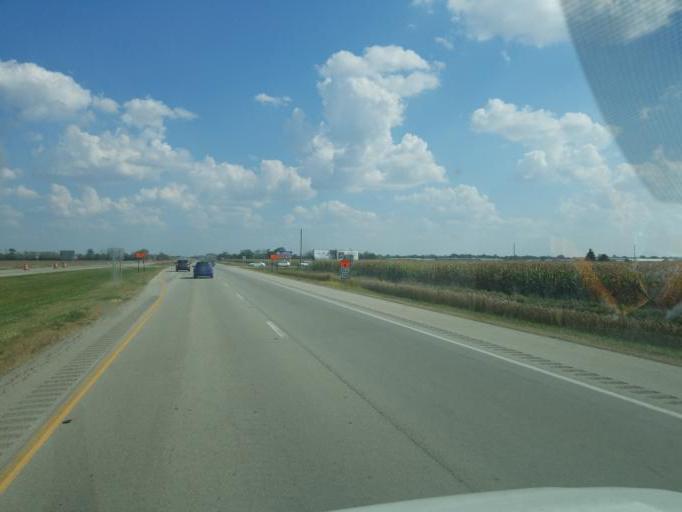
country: US
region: Ohio
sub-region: Van Wert County
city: Van Wert
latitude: 40.8911
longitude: -84.6122
